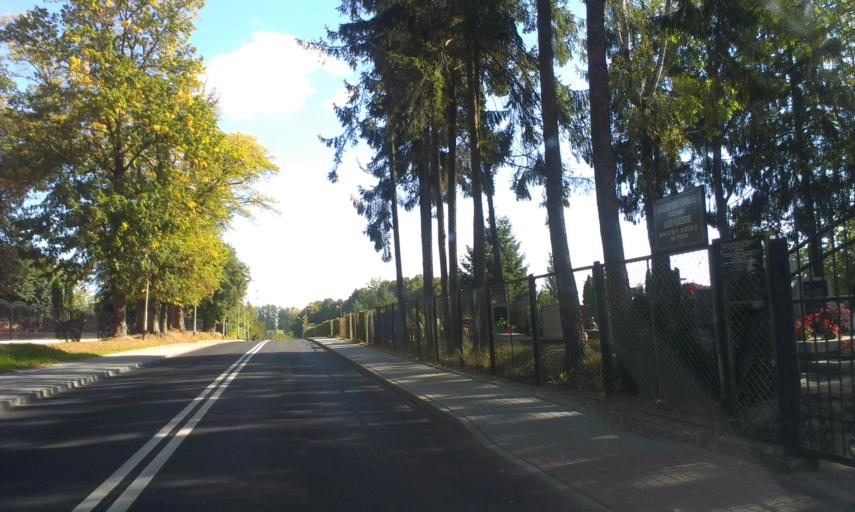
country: PL
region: West Pomeranian Voivodeship
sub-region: Powiat drawski
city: Czaplinek
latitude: 53.5623
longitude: 16.2372
